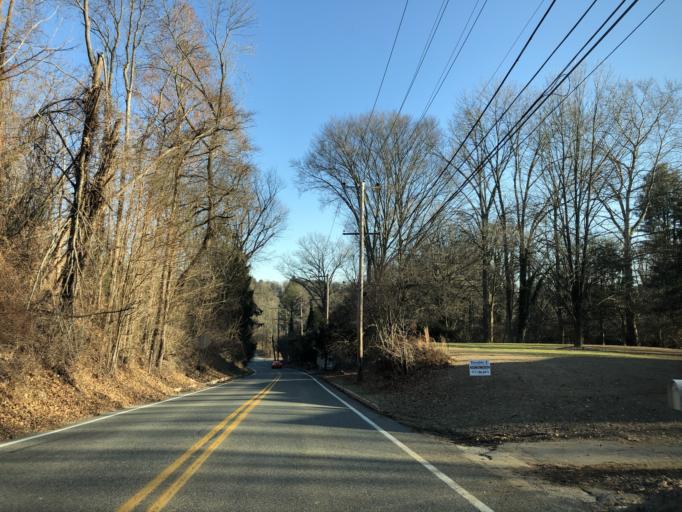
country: US
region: Pennsylvania
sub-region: Delaware County
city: Chester Heights
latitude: 39.8819
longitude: -75.5152
